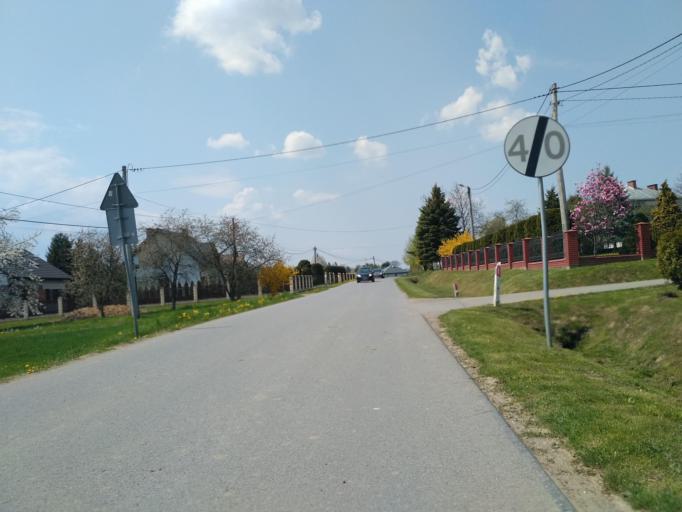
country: PL
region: Subcarpathian Voivodeship
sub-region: Powiat jasielski
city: Osiek Jasielski
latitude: 49.6711
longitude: 21.5357
